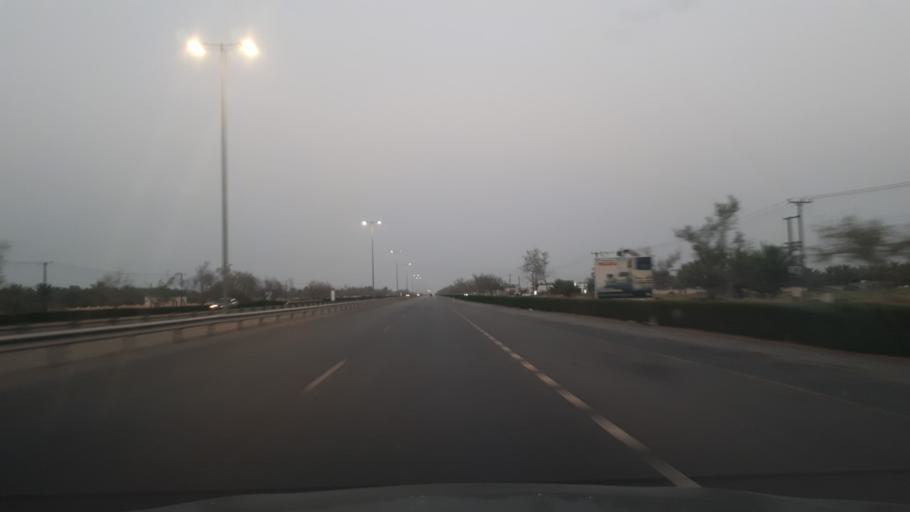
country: OM
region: Al Batinah
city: Barka'
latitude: 23.7337
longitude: 57.6861
